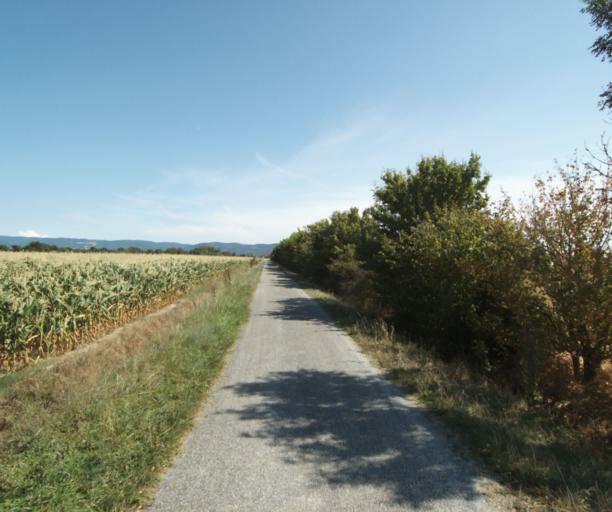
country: FR
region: Midi-Pyrenees
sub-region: Departement de la Haute-Garonne
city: Revel
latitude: 43.4865
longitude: 1.9738
